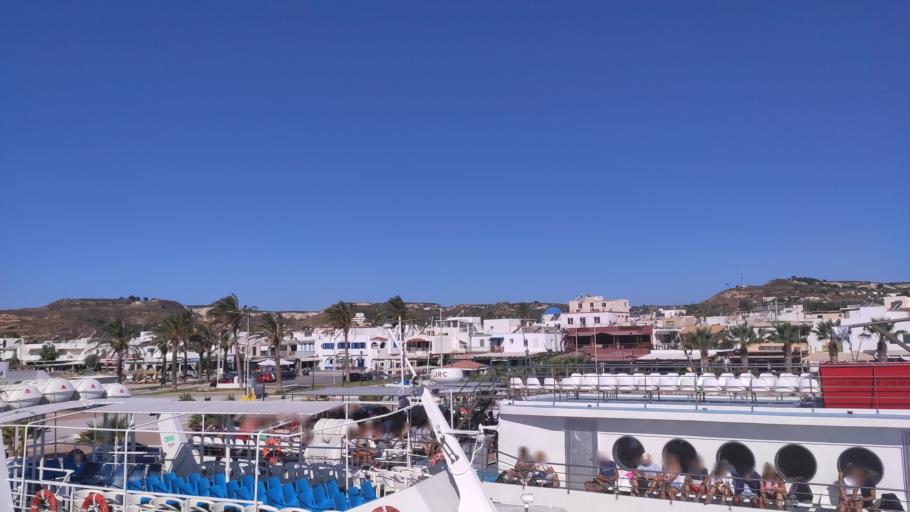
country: GR
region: South Aegean
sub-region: Nomos Dodekanisou
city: Kardamaina
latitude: 36.7812
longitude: 27.1445
